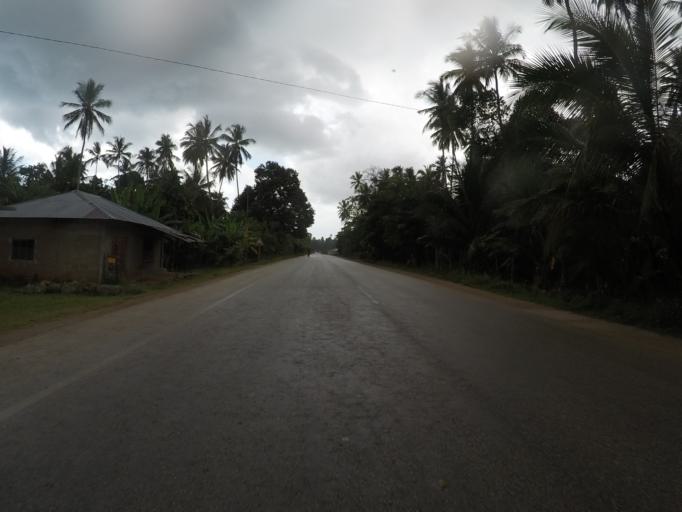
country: TZ
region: Zanzibar North
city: Mkokotoni
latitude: -5.9734
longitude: 39.1964
